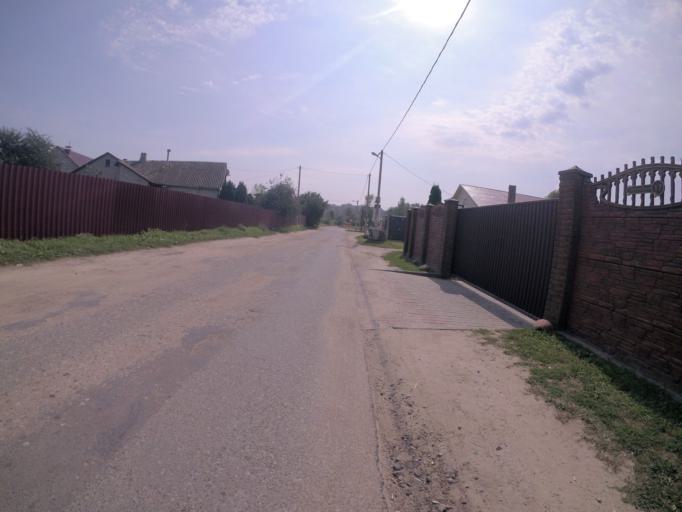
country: BY
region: Grodnenskaya
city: Hrodna
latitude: 53.7204
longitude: 23.8469
